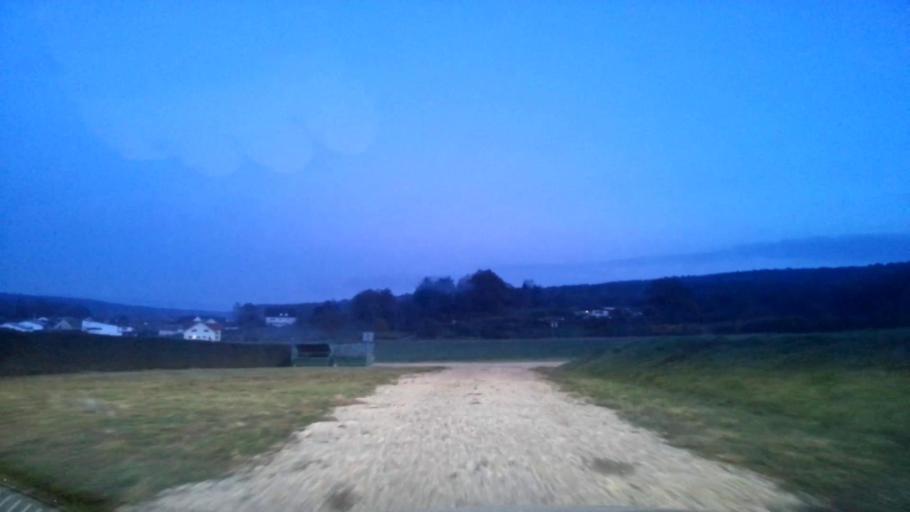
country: DE
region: Bavaria
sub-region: Upper Franconia
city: Frensdorf
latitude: 49.8480
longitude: 10.8877
